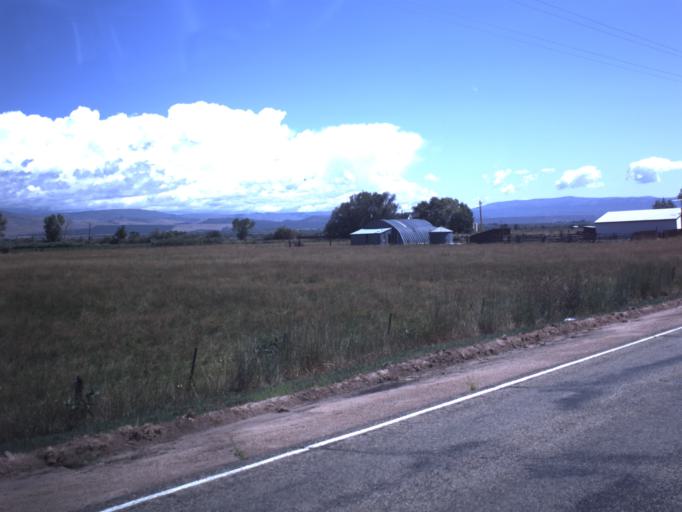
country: US
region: Utah
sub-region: Duchesne County
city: Roosevelt
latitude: 40.4329
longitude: -109.9757
